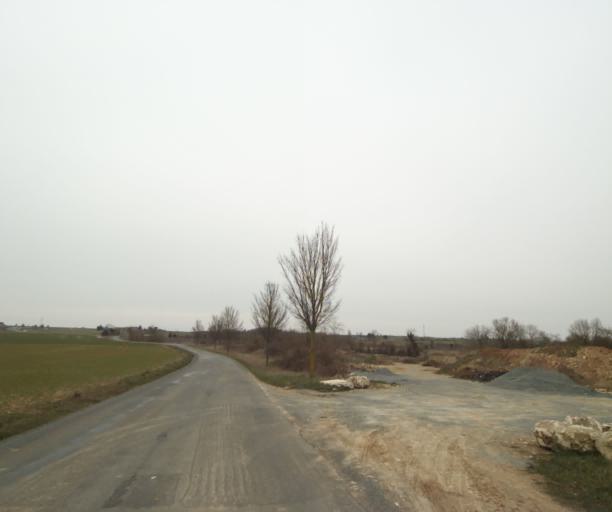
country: FR
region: Poitou-Charentes
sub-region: Departement des Deux-Sevres
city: Bessines
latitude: 46.3410
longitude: -0.5124
